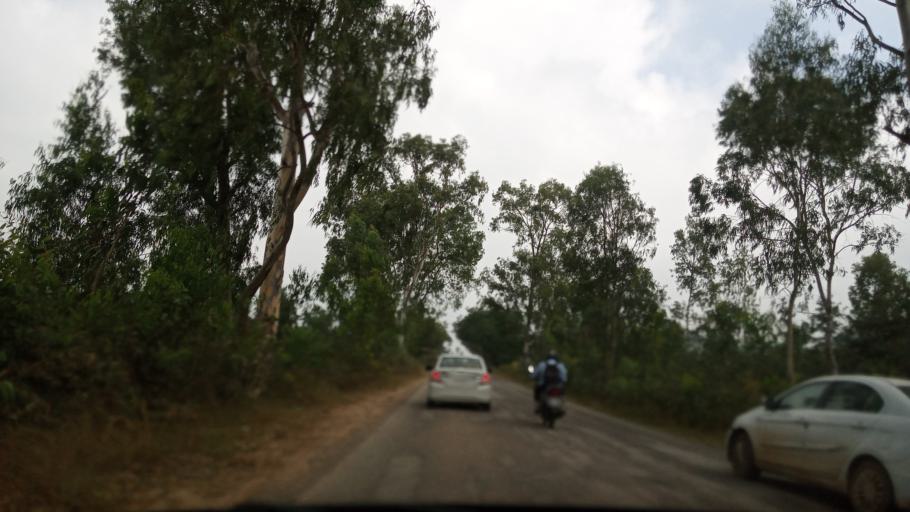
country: IN
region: Andhra Pradesh
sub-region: Chittoor
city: Madanapalle
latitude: 13.5092
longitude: 78.3359
